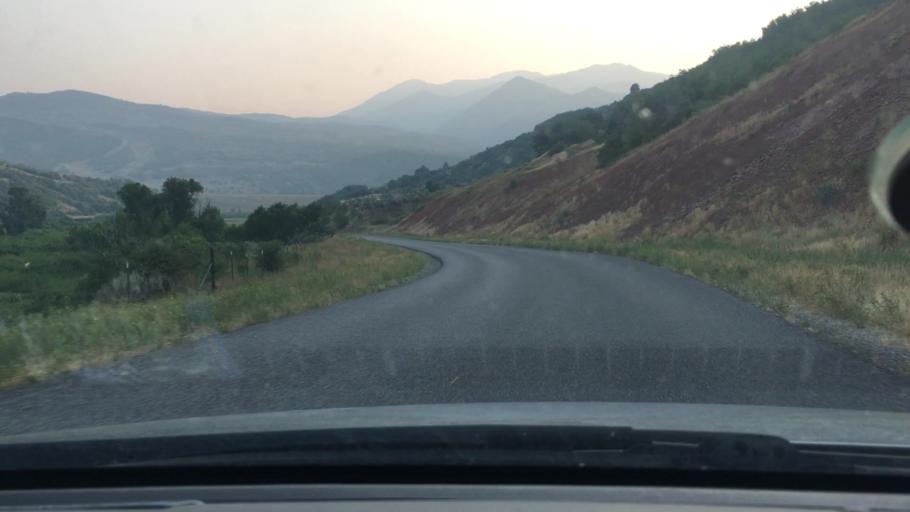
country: US
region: Utah
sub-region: Utah County
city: Mapleton
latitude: 40.0373
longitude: -111.4921
